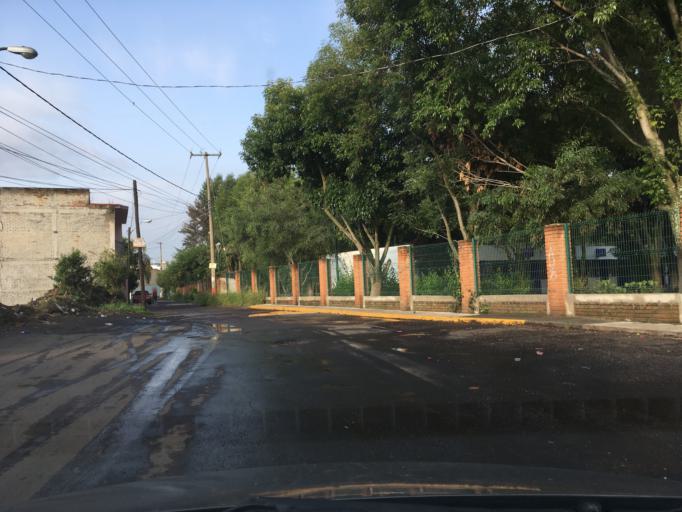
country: MX
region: Michoacan
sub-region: Morelia
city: Morelos
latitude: 19.6819
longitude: -101.2272
